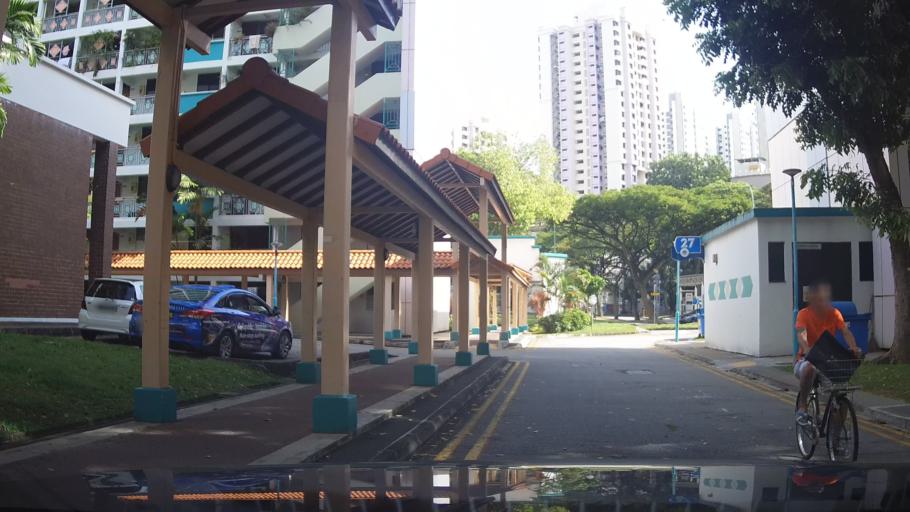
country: SG
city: Singapore
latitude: 1.3259
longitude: 103.8585
